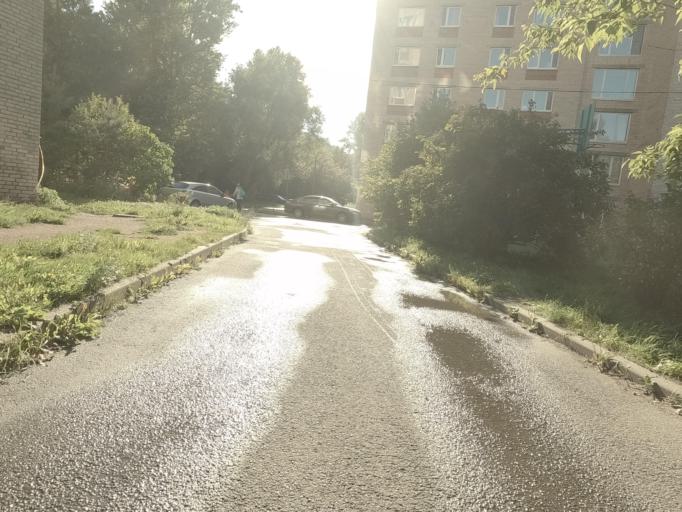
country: RU
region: St.-Petersburg
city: Krasnogvargeisky
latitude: 59.9327
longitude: 30.4255
